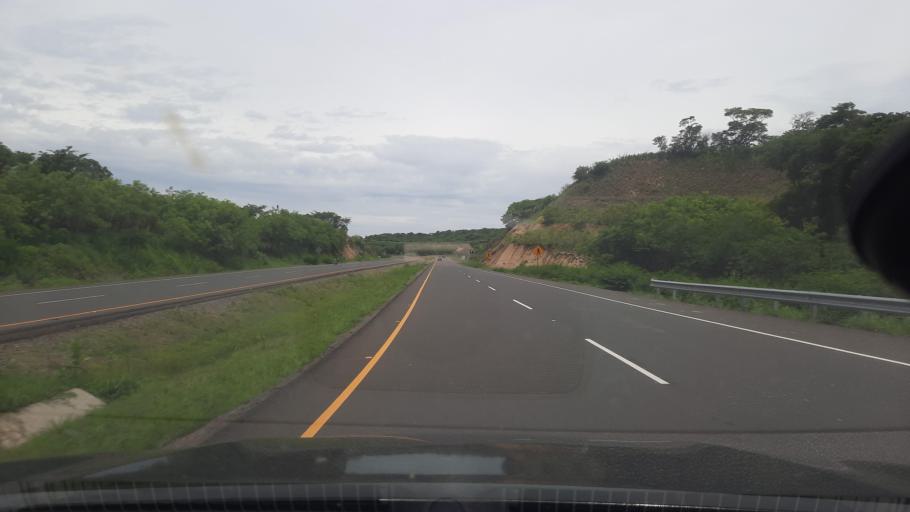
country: HN
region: Valle
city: Aramecina
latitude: 13.7572
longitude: -87.7138
